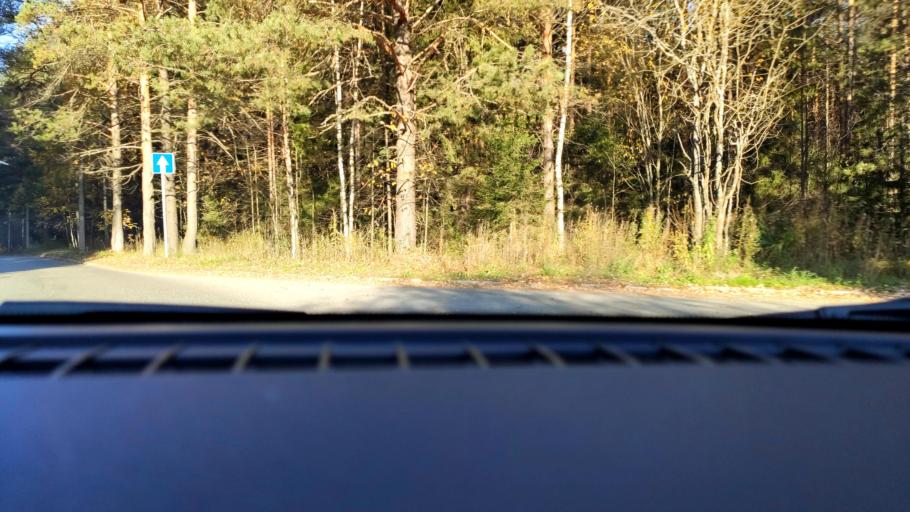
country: RU
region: Perm
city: Perm
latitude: 58.0547
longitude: 56.2299
